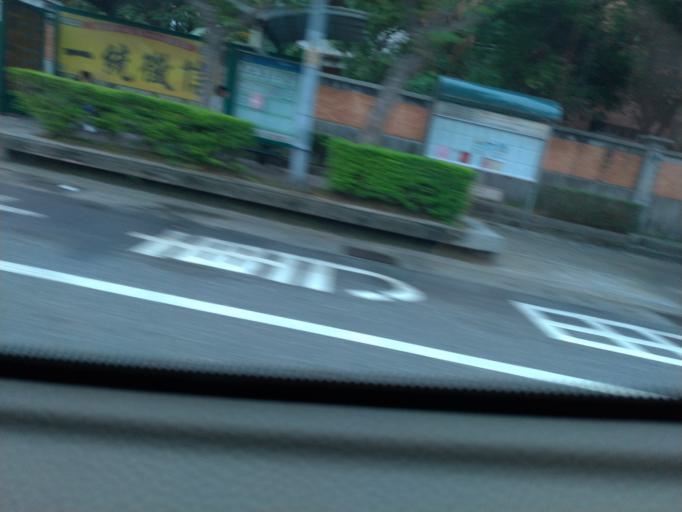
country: TW
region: Taiwan
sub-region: Taoyuan
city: Taoyuan
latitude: 24.9303
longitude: 121.3792
